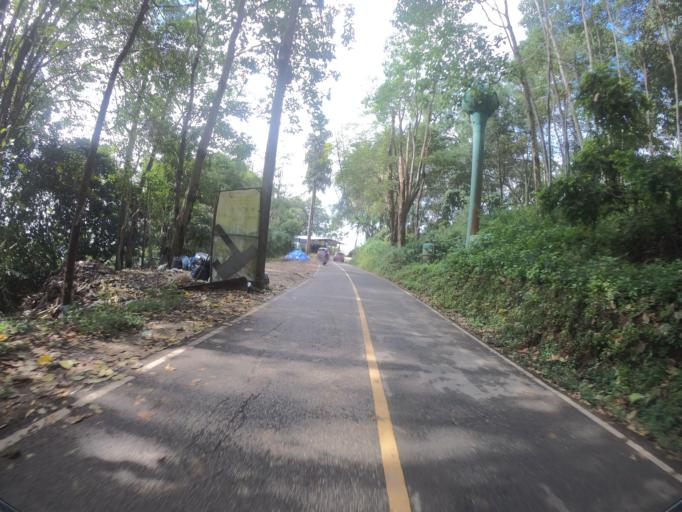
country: TH
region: Chiang Mai
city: Chiang Mai
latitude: 18.8141
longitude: 98.8824
